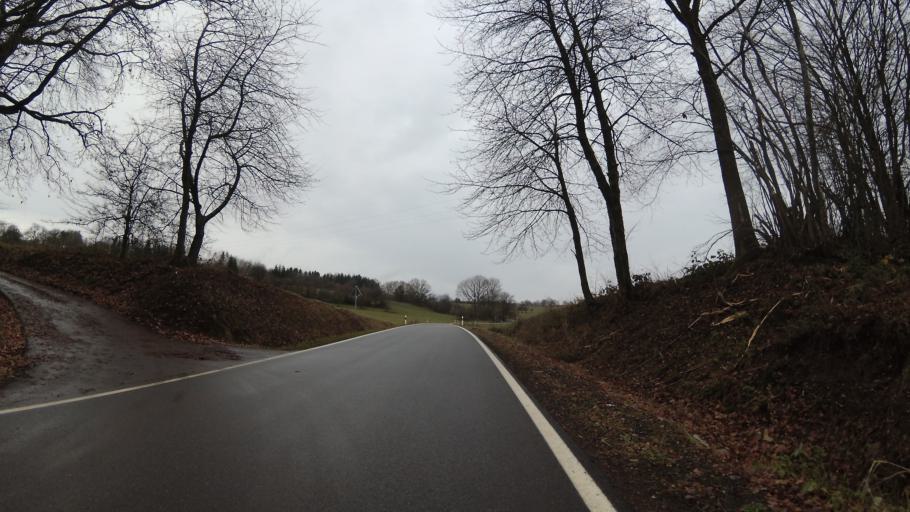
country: DE
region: Rheinland-Pfalz
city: Breitenbach
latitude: 49.4392
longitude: 7.2734
